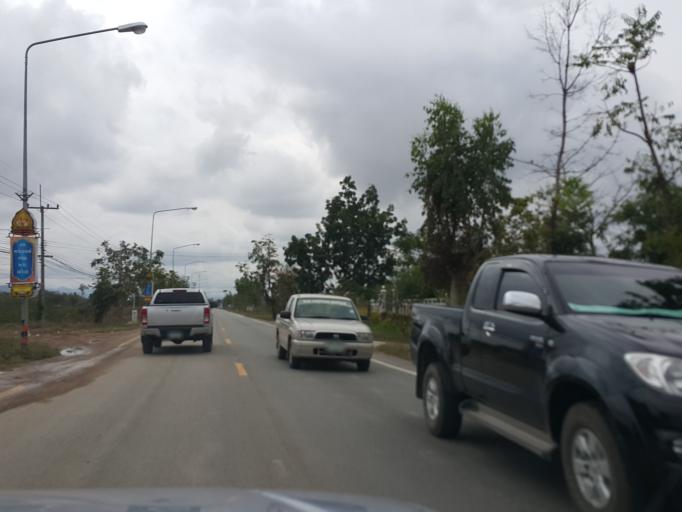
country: TH
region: Lamphun
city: Ban Thi
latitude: 18.5887
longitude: 99.0807
